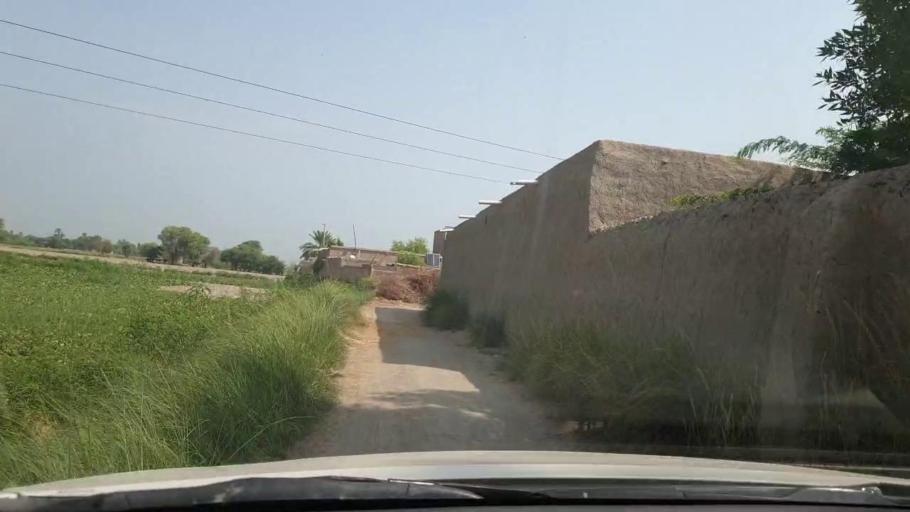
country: PK
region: Sindh
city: Shikarpur
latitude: 27.9755
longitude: 68.6708
